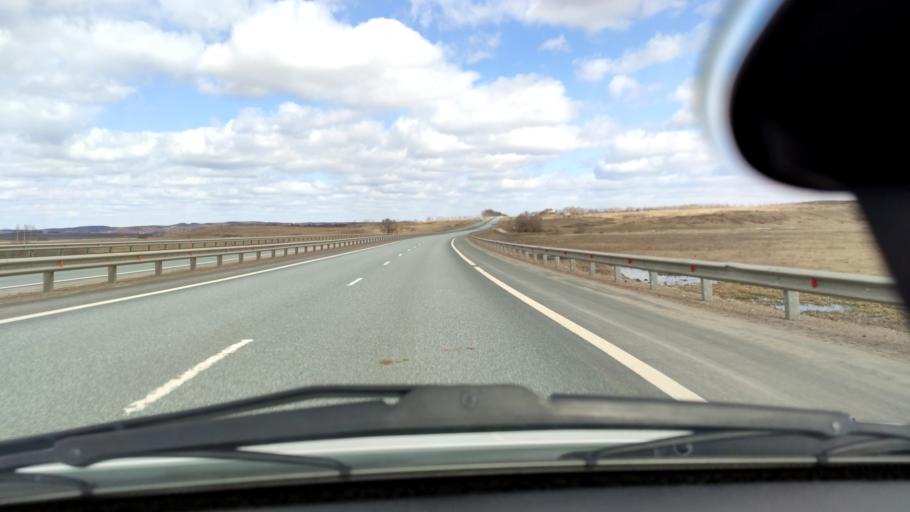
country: RU
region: Bashkortostan
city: Tolbazy
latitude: 54.3051
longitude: 55.8813
